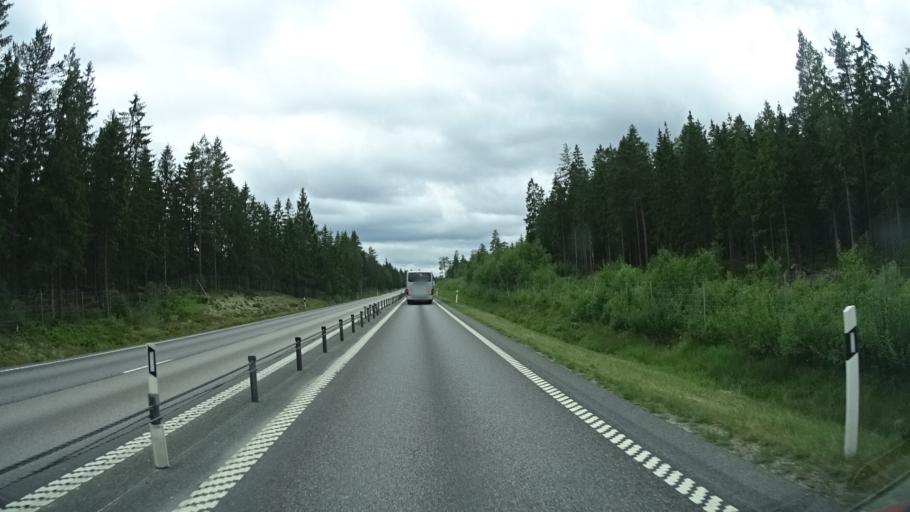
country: SE
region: Joenkoeping
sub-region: Varnamo Kommun
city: Rydaholm
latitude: 56.8988
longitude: 14.3308
